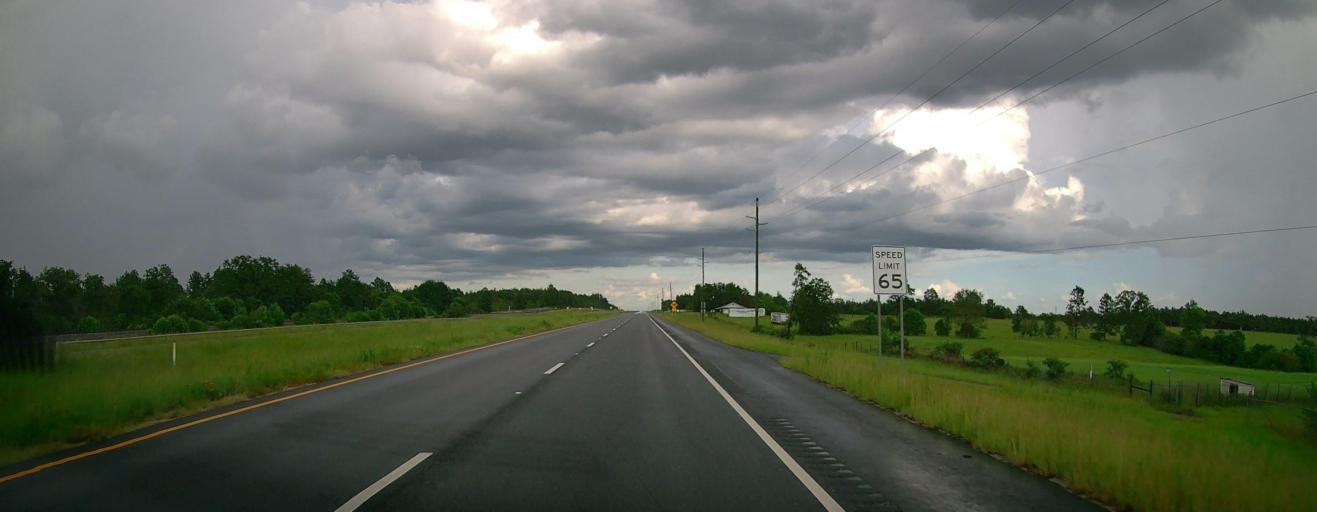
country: US
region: Georgia
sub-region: Taylor County
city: Butler
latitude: 32.5835
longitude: -84.3347
